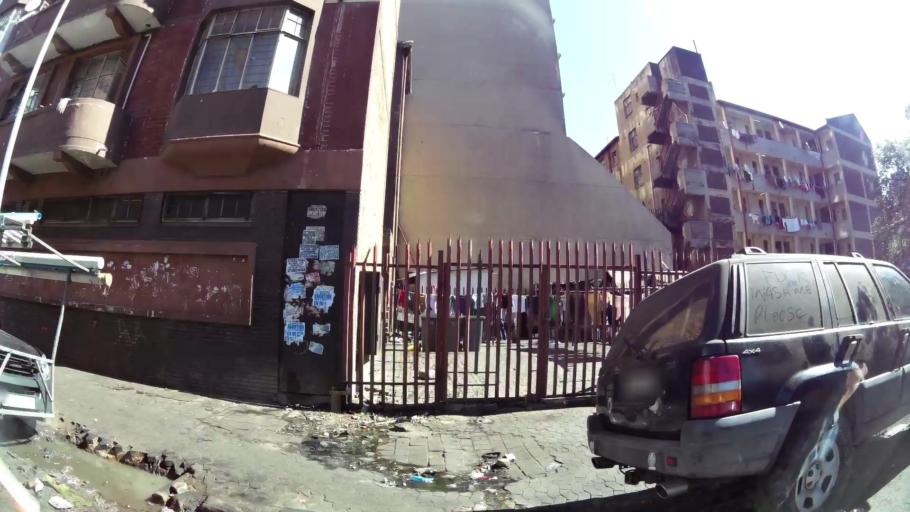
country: ZA
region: Gauteng
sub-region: City of Johannesburg Metropolitan Municipality
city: Johannesburg
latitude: -26.1995
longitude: 28.0514
